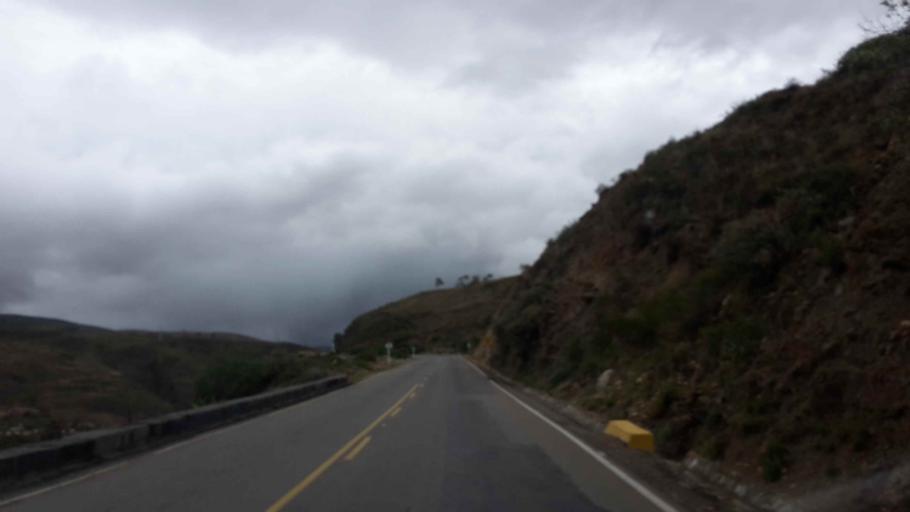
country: BO
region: Cochabamba
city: Punata
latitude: -17.4955
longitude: -65.7942
